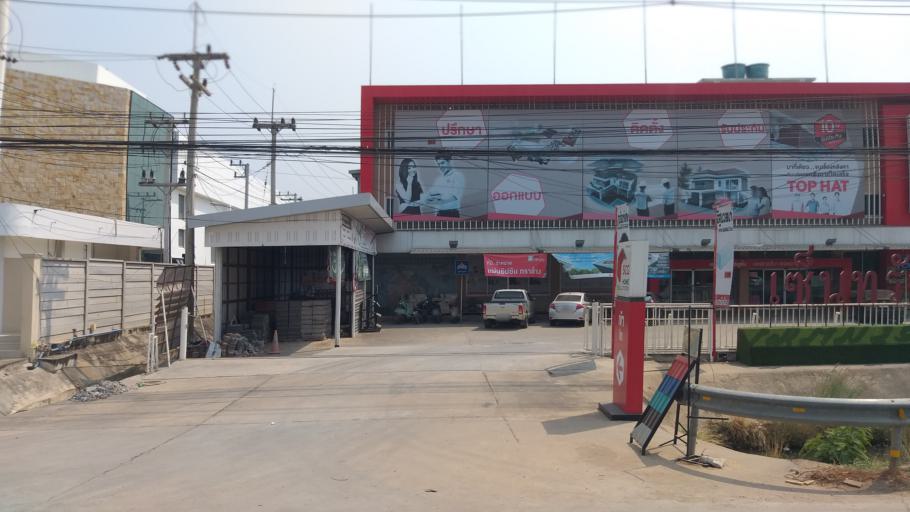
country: TH
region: Nakhon Ratchasima
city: Nakhon Ratchasima
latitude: 15.0482
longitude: 102.1545
